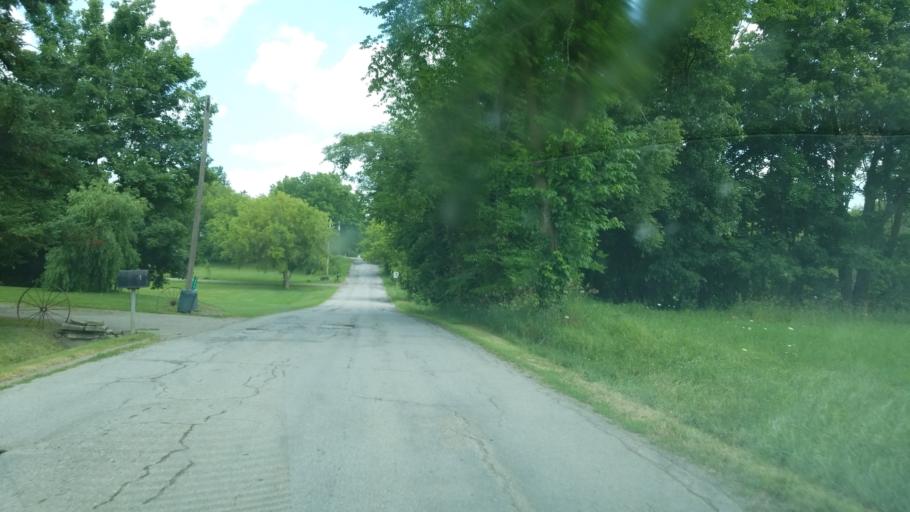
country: US
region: Michigan
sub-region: Kent County
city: Cedar Springs
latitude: 43.2890
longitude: -85.5115
